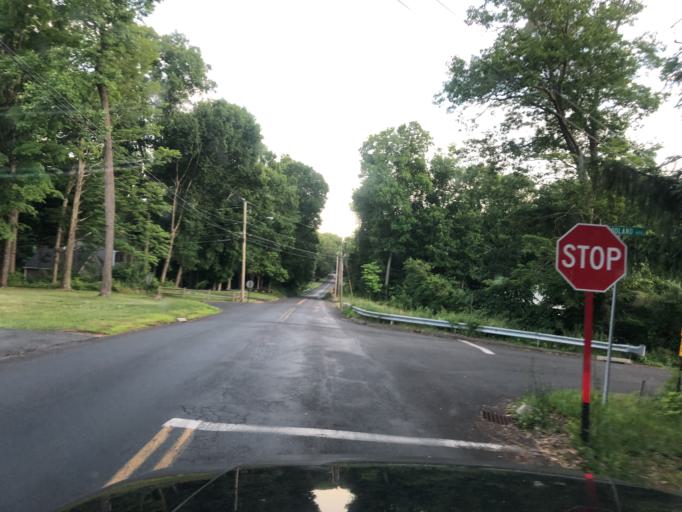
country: US
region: Connecticut
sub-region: Middlesex County
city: Middletown
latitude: 41.5409
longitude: -72.7022
